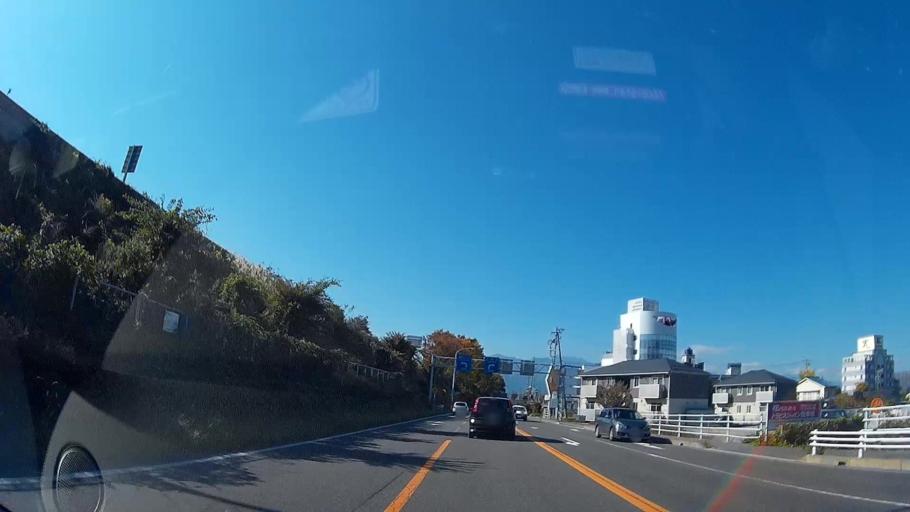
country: JP
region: Nagano
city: Matsumoto
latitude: 36.1700
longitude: 137.9503
